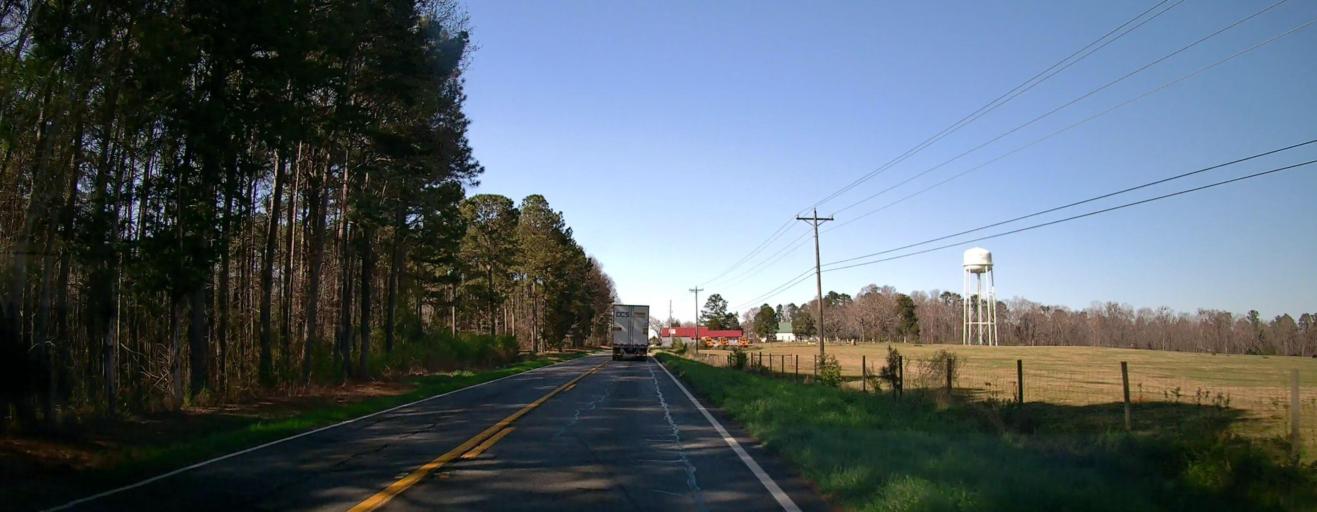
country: US
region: Georgia
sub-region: Butts County
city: Indian Springs
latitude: 33.1743
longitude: -83.9588
